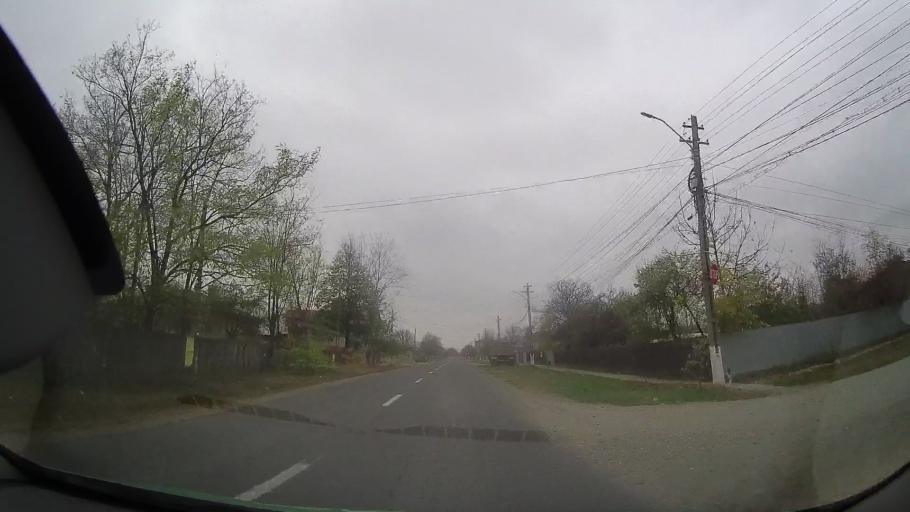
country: RO
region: Ialomita
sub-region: Comuna Garbovi
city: Garbovi
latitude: 44.7838
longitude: 26.7669
